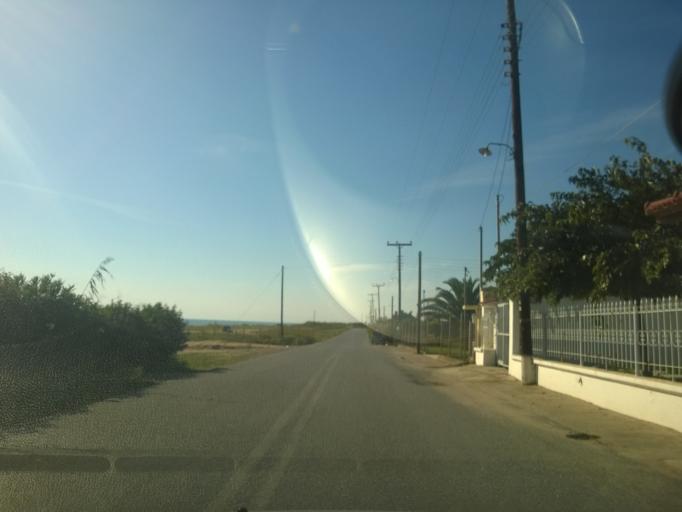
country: GR
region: Central Macedonia
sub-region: Nomos Chalkidikis
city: Nea Kallikrateia
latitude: 40.3201
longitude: 23.0358
